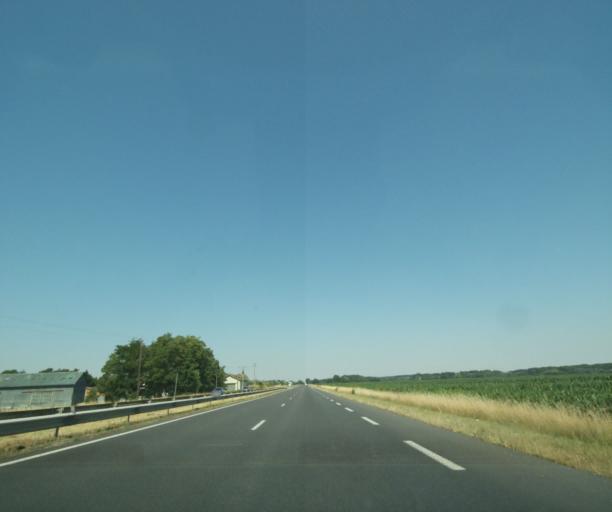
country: FR
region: Champagne-Ardenne
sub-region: Departement de la Haute-Marne
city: Villiers-en-Lieu
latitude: 48.6626
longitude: 4.7957
